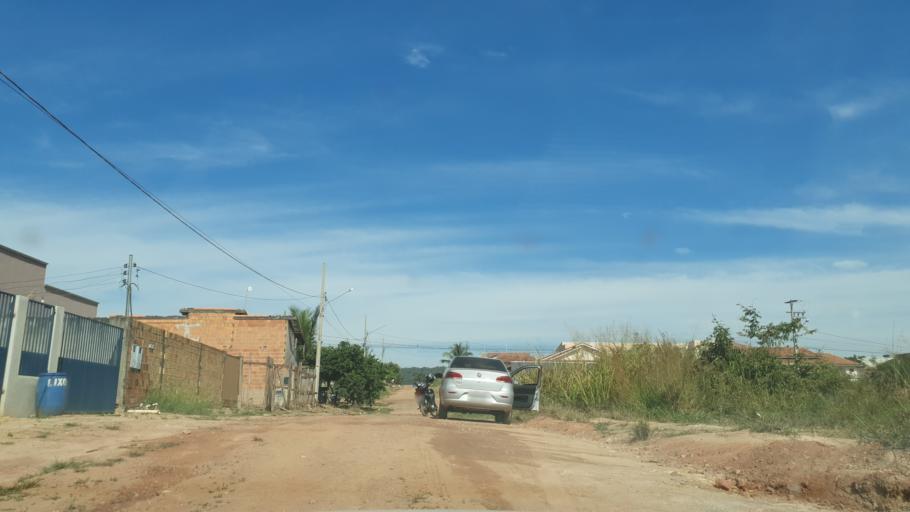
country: BR
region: Mato Grosso
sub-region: Pontes E Lacerda
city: Pontes e Lacerda
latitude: -15.2544
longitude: -59.3124
